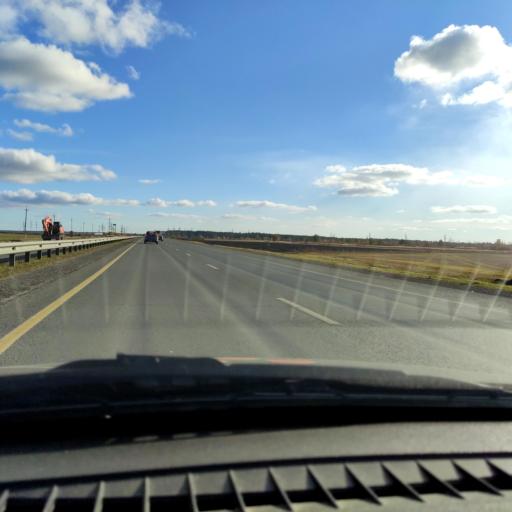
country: RU
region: Samara
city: Zhigulevsk
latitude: 53.5532
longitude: 49.5051
